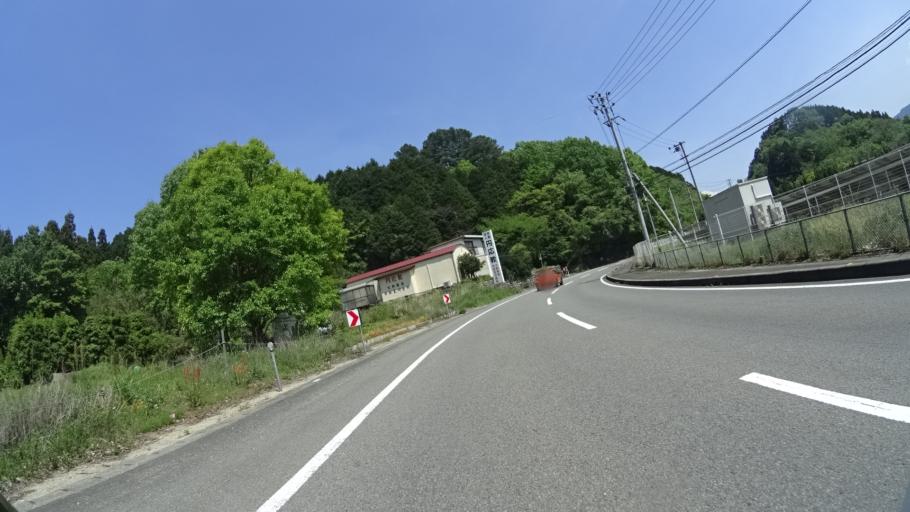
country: JP
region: Ehime
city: Hojo
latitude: 33.9967
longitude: 132.9235
